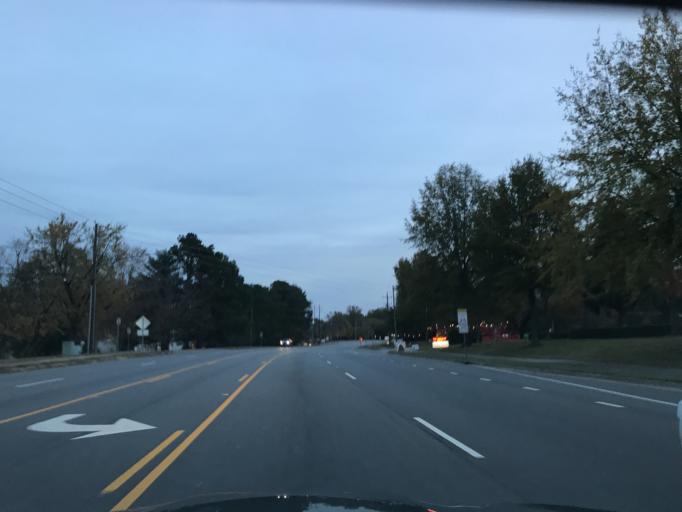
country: US
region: North Carolina
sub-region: Wake County
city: West Raleigh
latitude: 35.8599
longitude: -78.6181
